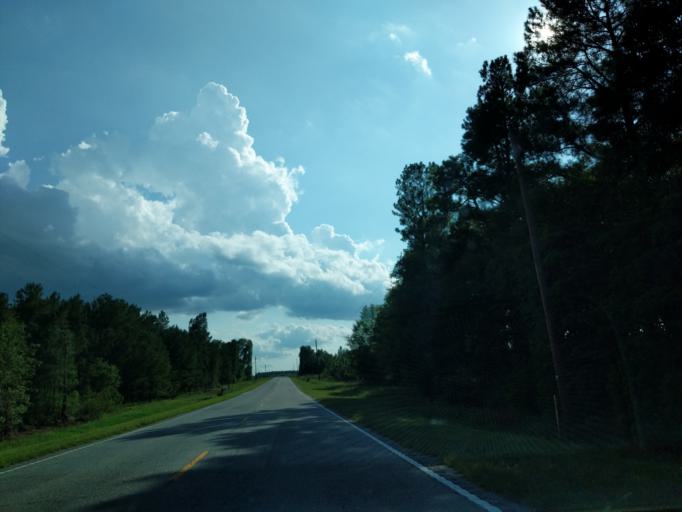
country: US
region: South Carolina
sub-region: Barnwell County
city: Williston
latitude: 33.4306
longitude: -81.3889
